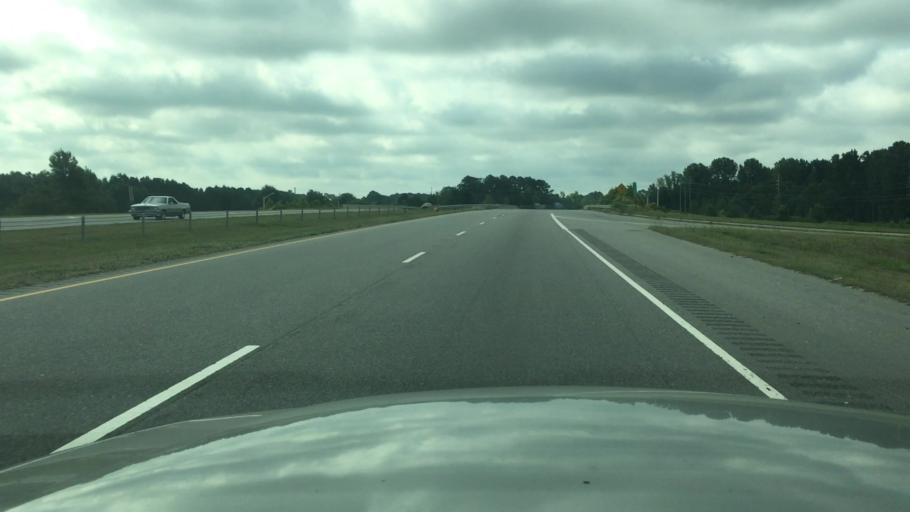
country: US
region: North Carolina
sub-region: Cumberland County
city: Fayetteville
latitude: 35.0338
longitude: -78.8784
